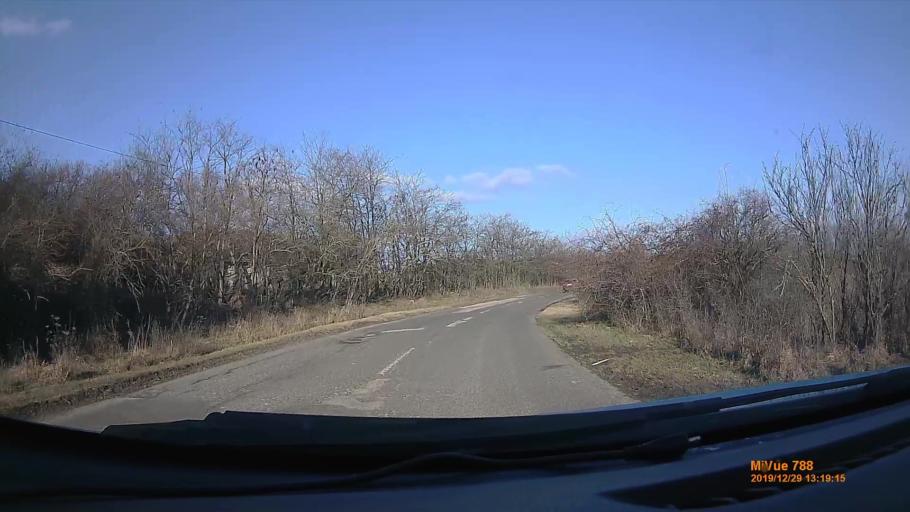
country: HU
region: Heves
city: Domoszlo
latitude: 47.8442
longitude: 20.1300
